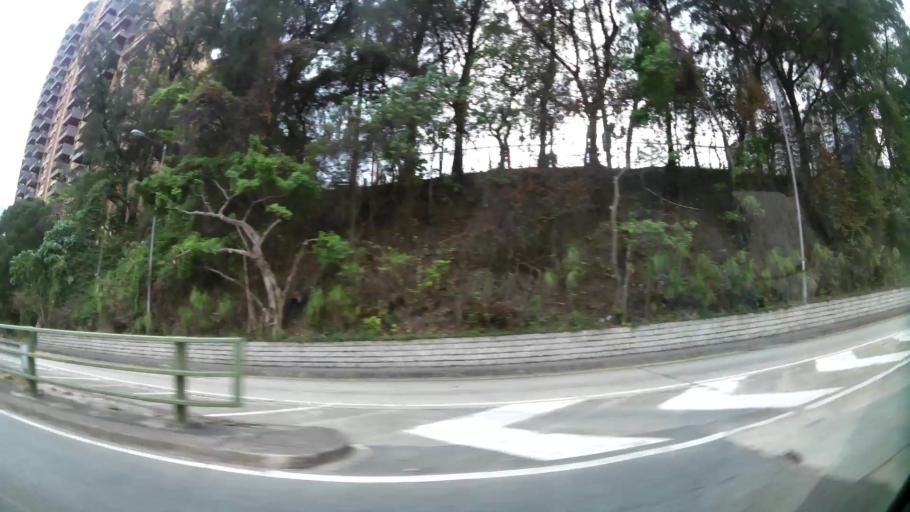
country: HK
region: Kowloon City
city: Kowloon
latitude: 22.3085
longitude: 114.1790
